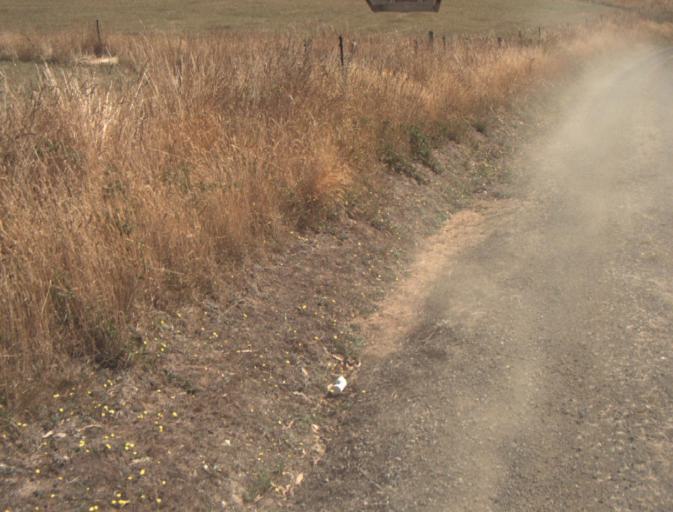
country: AU
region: Tasmania
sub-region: Launceston
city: Mayfield
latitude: -41.2062
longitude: 147.2182
